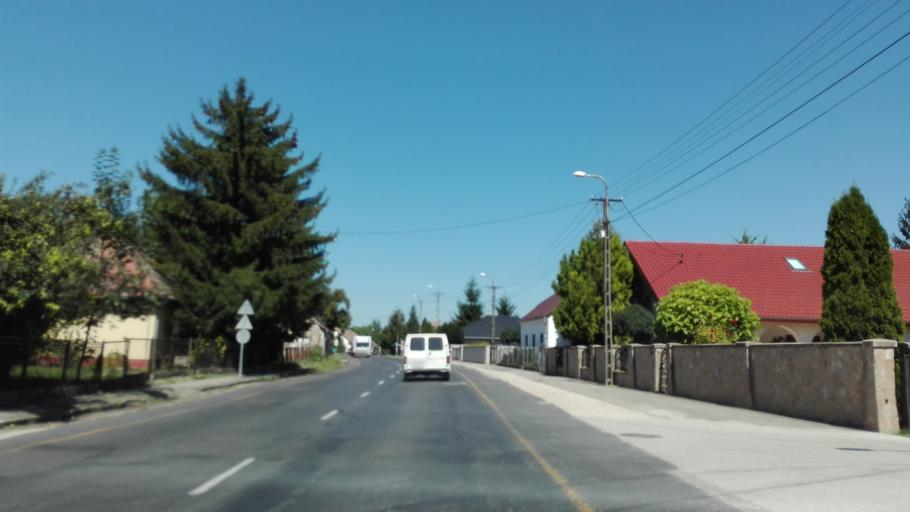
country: HU
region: Fejer
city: Mezoszilas
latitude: 46.8106
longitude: 18.4835
